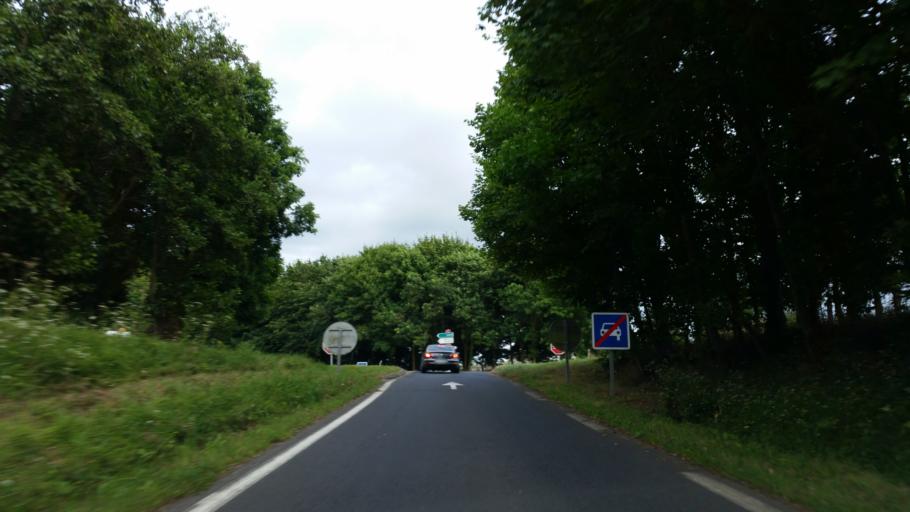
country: FR
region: Lower Normandy
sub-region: Departement du Calvados
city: Le Molay-Littry
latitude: 49.3315
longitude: -0.9012
